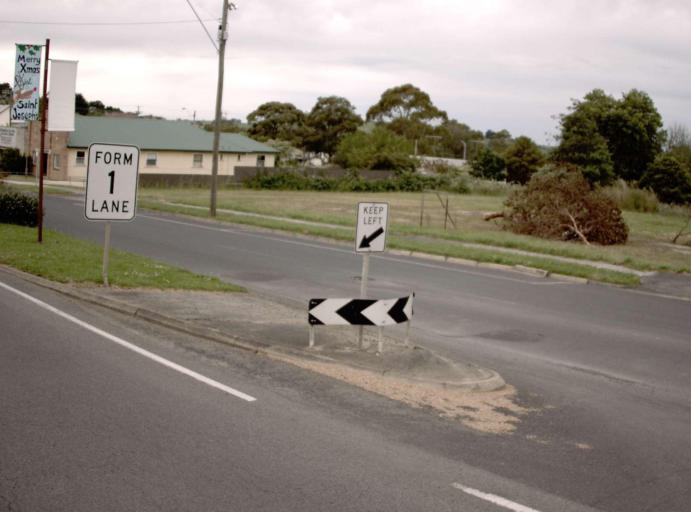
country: AU
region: Victoria
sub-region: Bass Coast
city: North Wonthaggi
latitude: -38.4354
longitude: 145.8267
